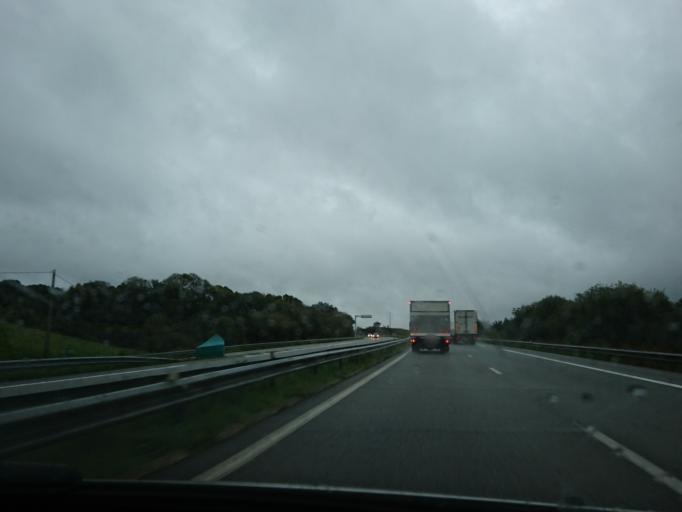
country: FR
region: Brittany
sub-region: Departement du Finistere
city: Chateaulin
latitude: 48.2382
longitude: -4.1057
